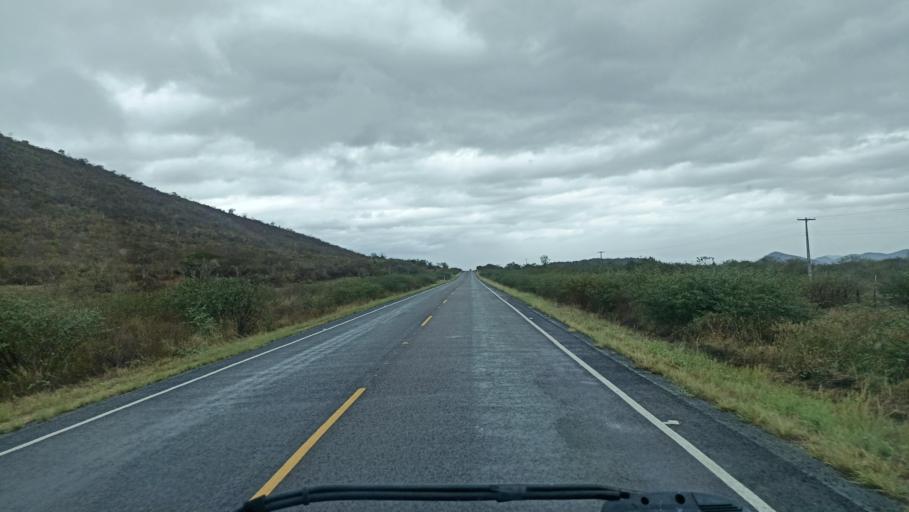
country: BR
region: Bahia
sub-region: Iacu
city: Iacu
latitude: -12.9575
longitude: -40.4708
